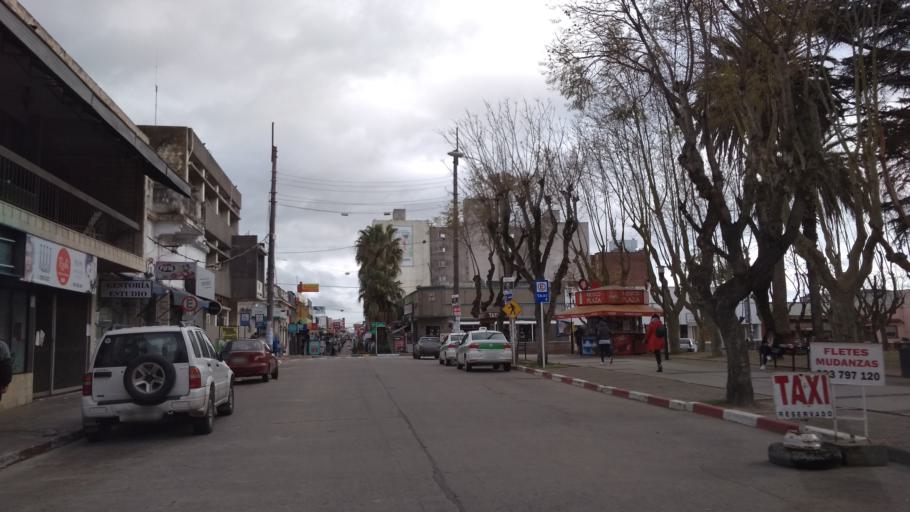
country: UY
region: Canelones
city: Pando
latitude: -34.7219
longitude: -55.9598
